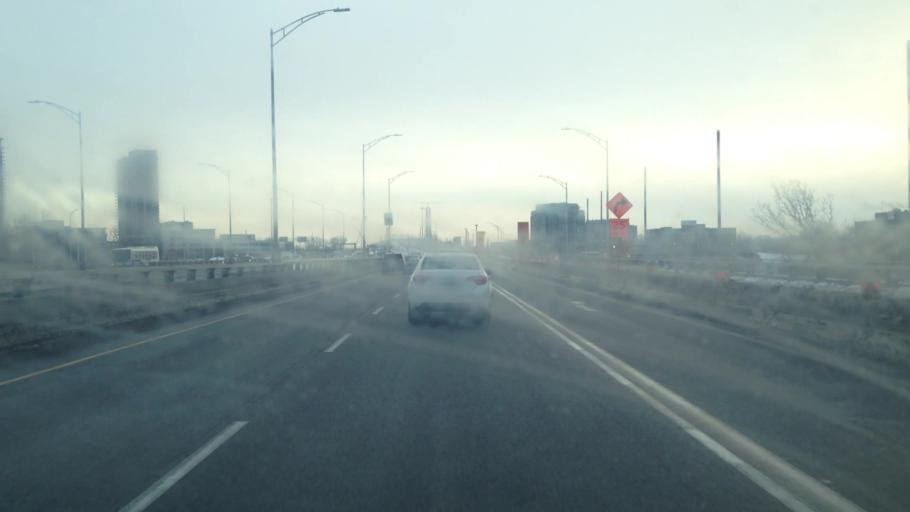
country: CA
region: Quebec
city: Westmount
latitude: 45.4707
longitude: -73.5490
